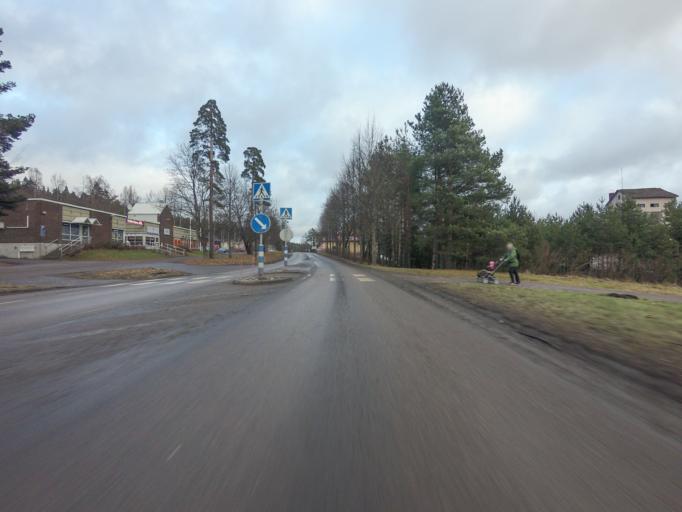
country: FI
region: Uusimaa
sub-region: Helsinki
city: Lohja
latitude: 60.2671
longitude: 24.1204
